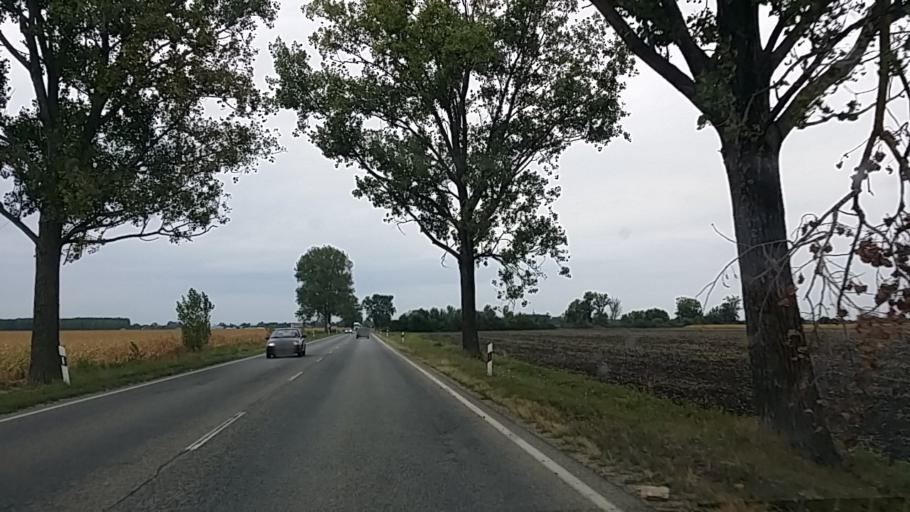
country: HU
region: Gyor-Moson-Sopron
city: Kapuvar
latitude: 47.5894
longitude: 17.0709
